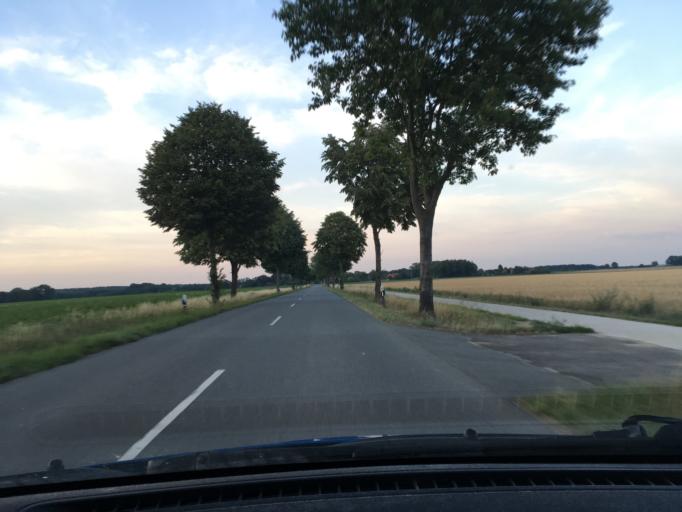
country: DE
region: Lower Saxony
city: Jelmstorf
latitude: 53.1347
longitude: 10.5405
